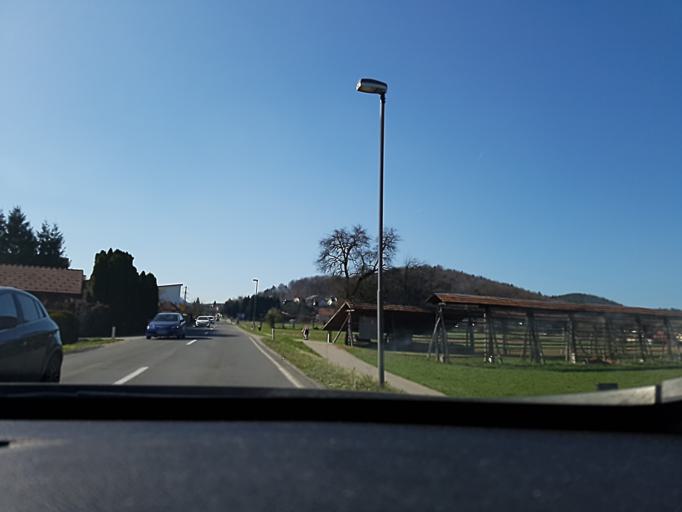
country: SI
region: Trzin
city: Trzin
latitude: 46.1025
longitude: 14.5493
